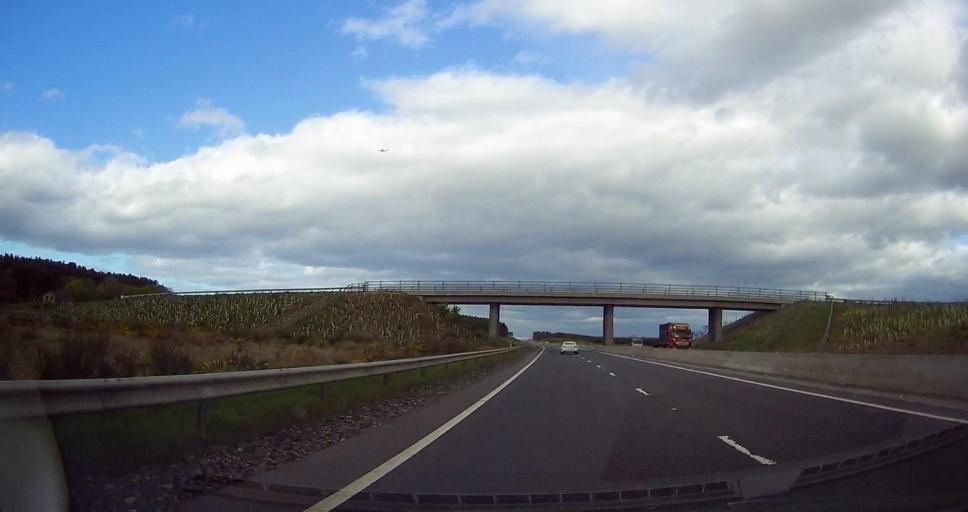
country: GB
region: Scotland
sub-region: Aberdeenshire
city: Portlethen
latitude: 57.0854
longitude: -2.1440
